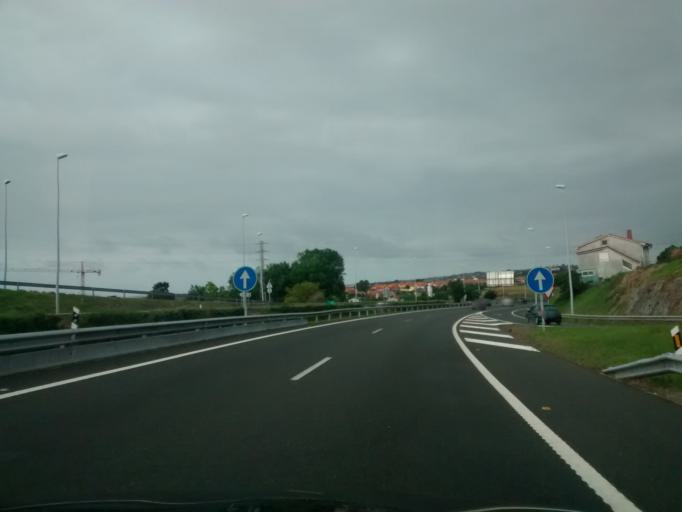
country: ES
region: Cantabria
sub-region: Provincia de Cantabria
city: Santa Cruz de Bezana
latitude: 43.4611
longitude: -3.8613
